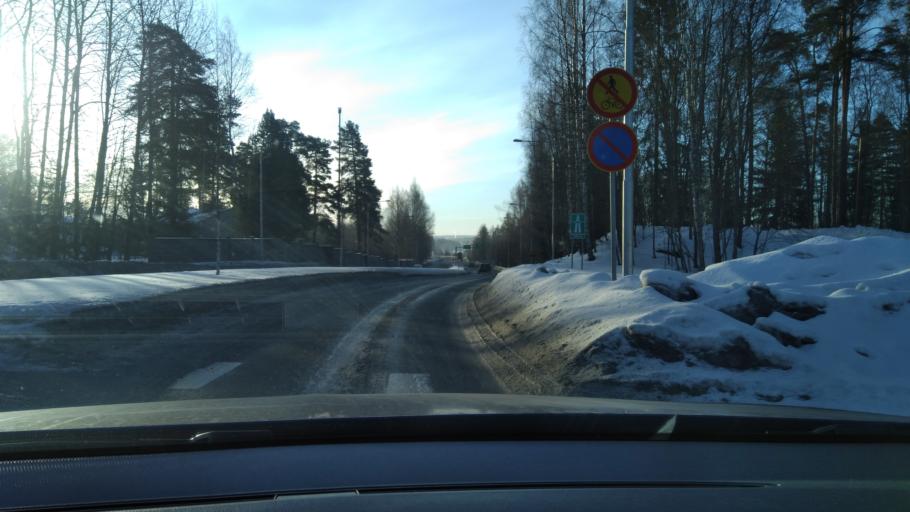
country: FI
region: Pirkanmaa
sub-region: Tampere
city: Pirkkala
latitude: 61.5006
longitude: 23.6484
